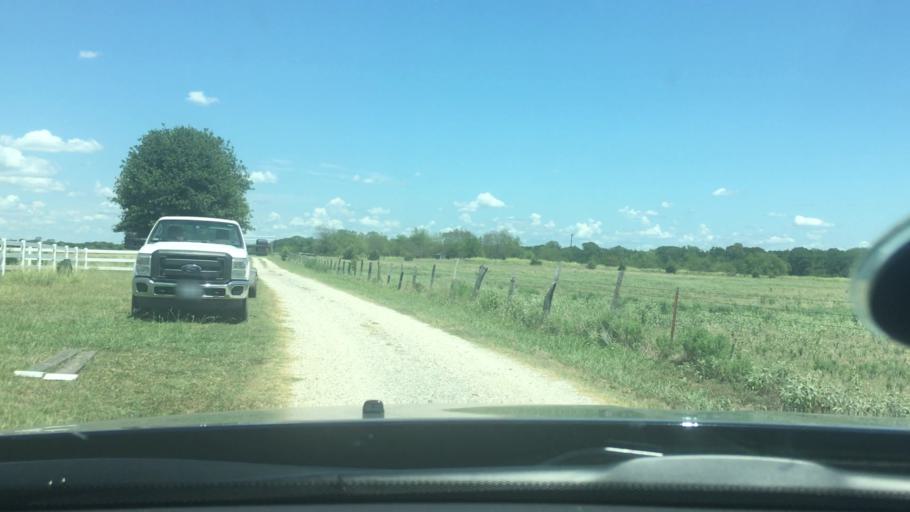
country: US
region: Oklahoma
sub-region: Bryan County
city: Durant
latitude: 33.9951
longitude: -96.0969
